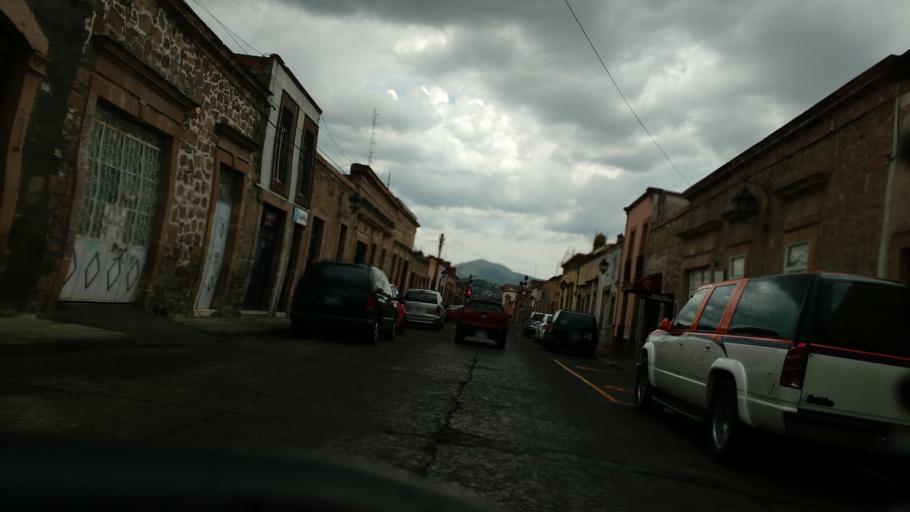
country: MX
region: Michoacan
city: Morelia
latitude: 19.7057
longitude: -101.1864
